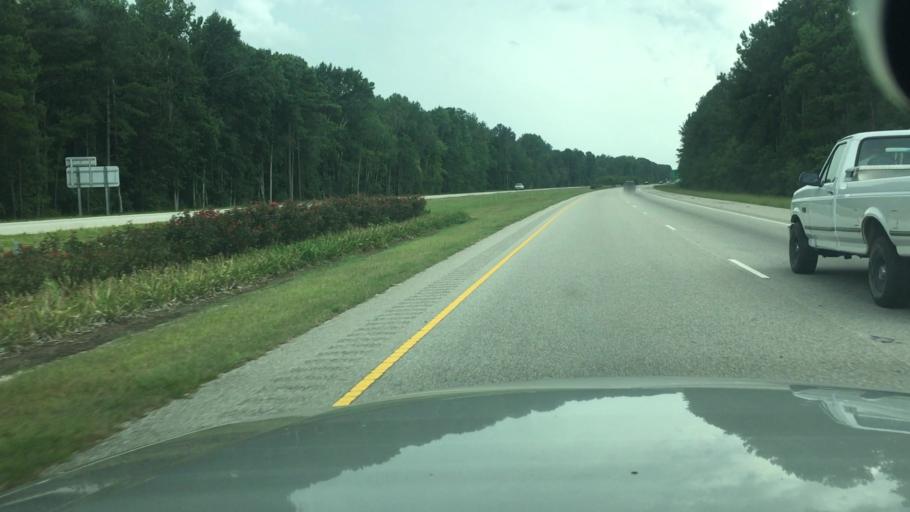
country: US
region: North Carolina
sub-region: Cumberland County
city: Fayetteville
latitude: 34.9974
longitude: -78.8637
